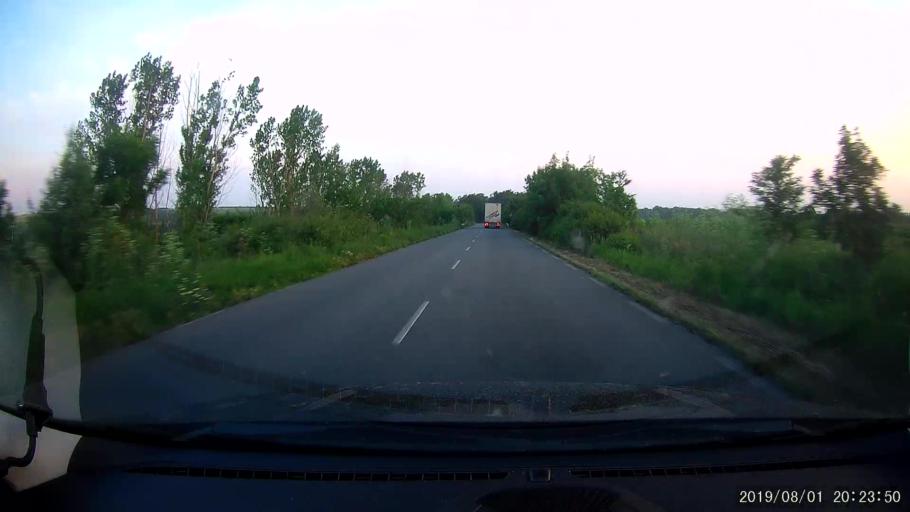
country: BG
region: Yambol
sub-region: Obshtina Elkhovo
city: Elkhovo
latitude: 42.2414
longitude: 26.5975
